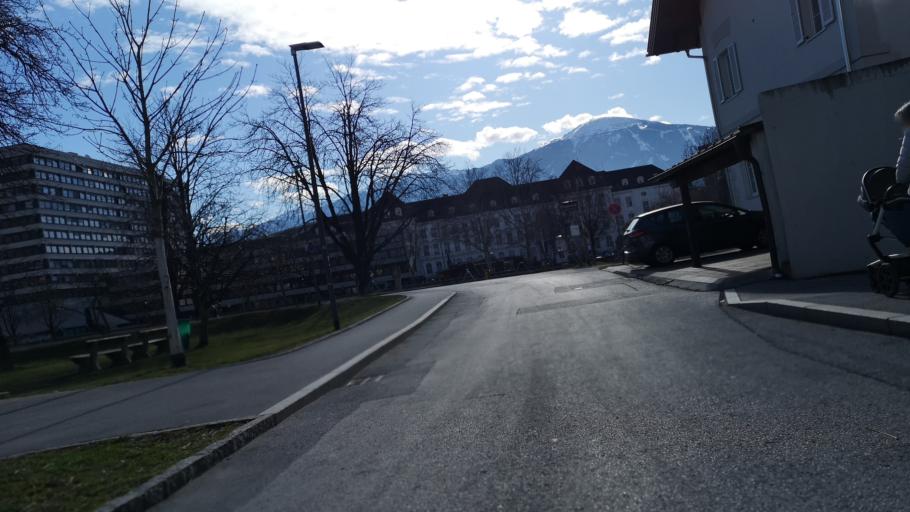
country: AT
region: Tyrol
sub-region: Innsbruck Stadt
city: Innsbruck
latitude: 47.2643
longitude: 11.3819
